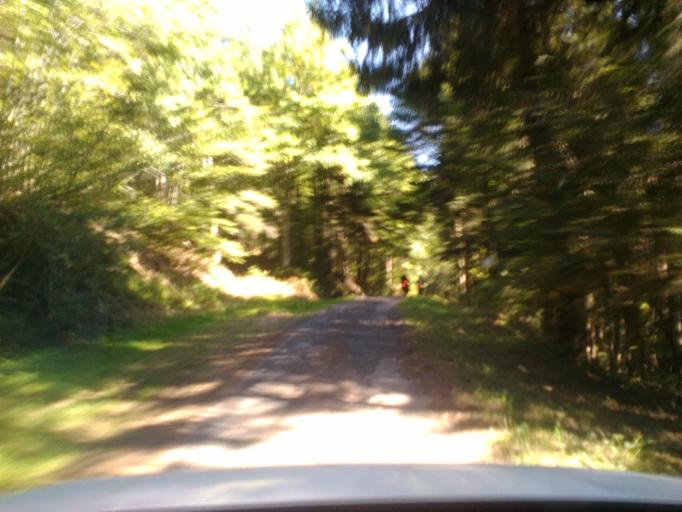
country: FR
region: Lorraine
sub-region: Departement des Vosges
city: Sainte-Marguerite
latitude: 48.3168
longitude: 6.9897
